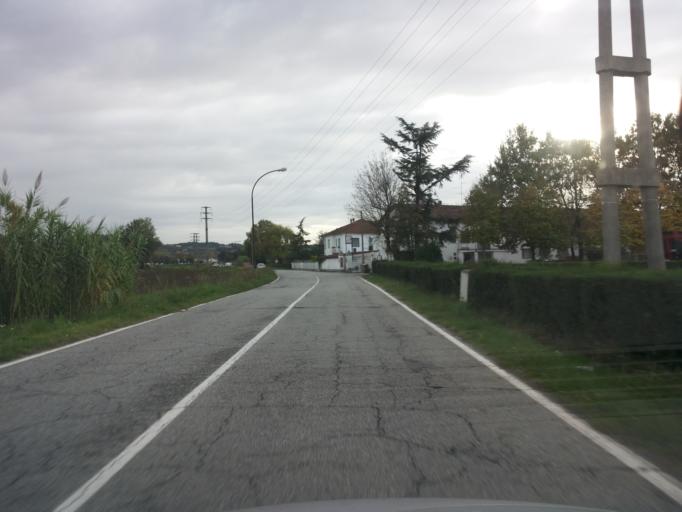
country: IT
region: Piedmont
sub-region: Provincia di Alessandria
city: Casale Monferrato
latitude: 45.1146
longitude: 8.4415
